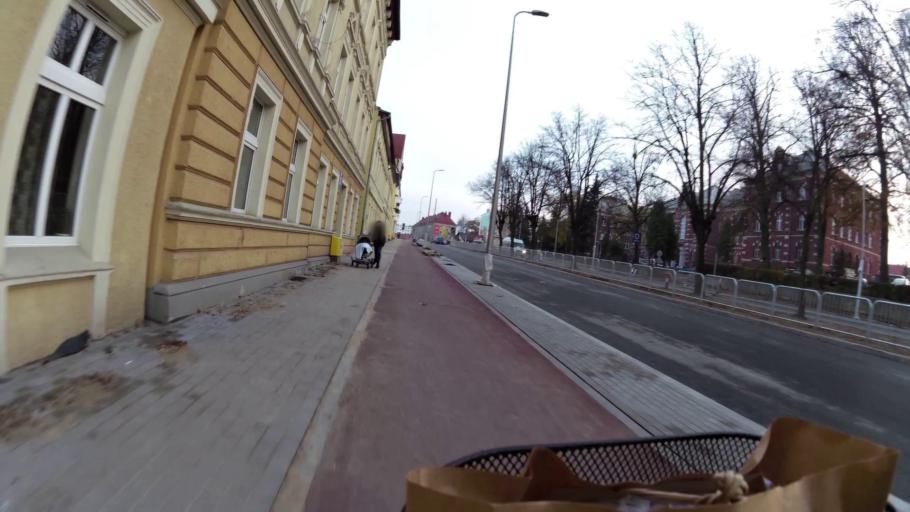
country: PL
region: West Pomeranian Voivodeship
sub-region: Koszalin
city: Koszalin
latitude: 54.1858
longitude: 16.1758
